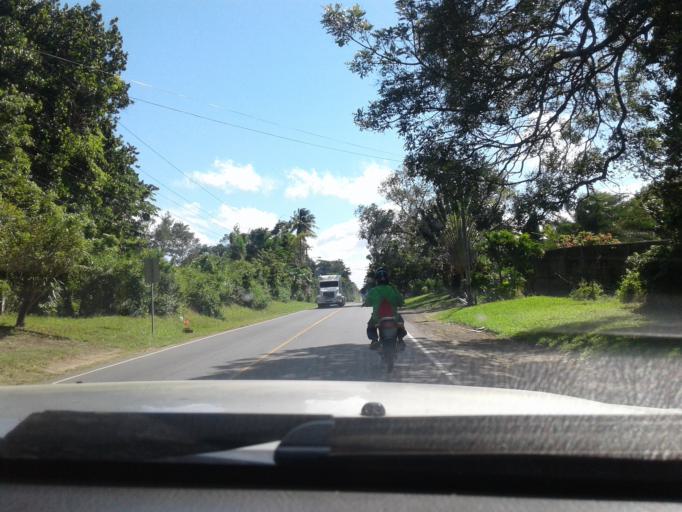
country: NI
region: Carazo
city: La Paz de Oriente
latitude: 11.8254
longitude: -86.1663
